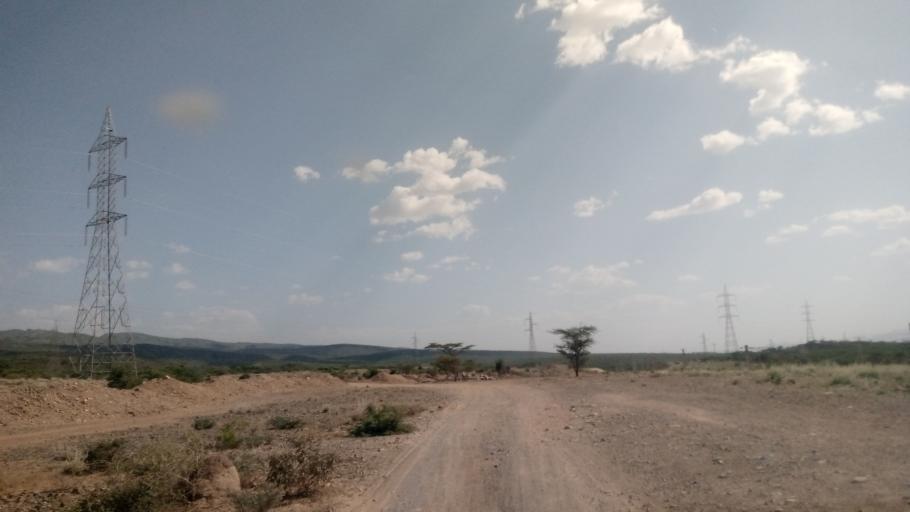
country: ET
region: Oromiya
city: Hirna
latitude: 9.5452
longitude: 41.1519
